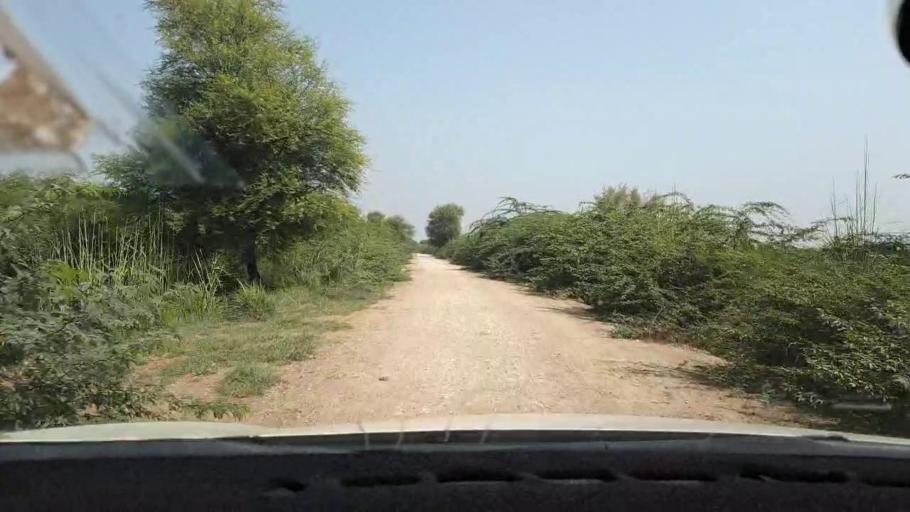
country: PK
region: Sindh
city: Tando Mittha Khan
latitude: 25.9487
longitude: 69.2985
